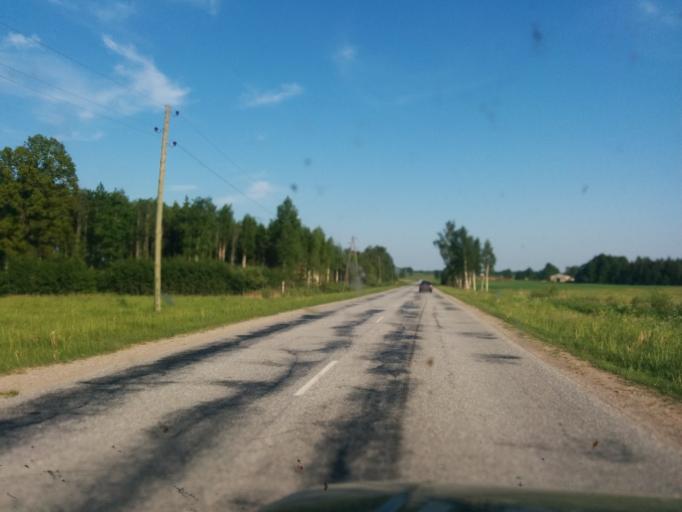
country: LV
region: Talsu Rajons
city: Talsi
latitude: 57.3009
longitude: 22.5562
